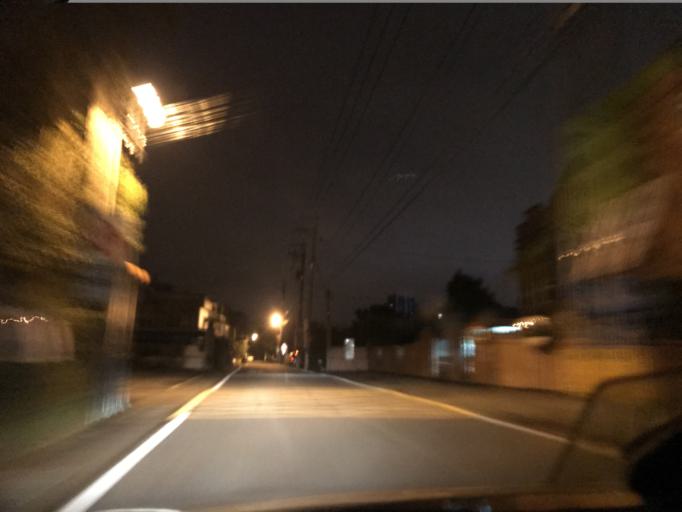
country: TW
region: Taiwan
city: Daxi
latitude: 24.8534
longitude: 121.2146
